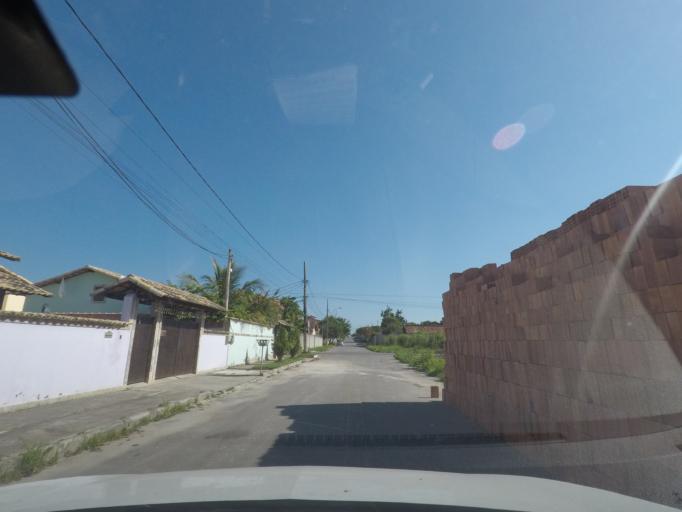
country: BR
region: Rio de Janeiro
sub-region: Marica
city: Marica
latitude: -22.9666
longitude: -42.9190
